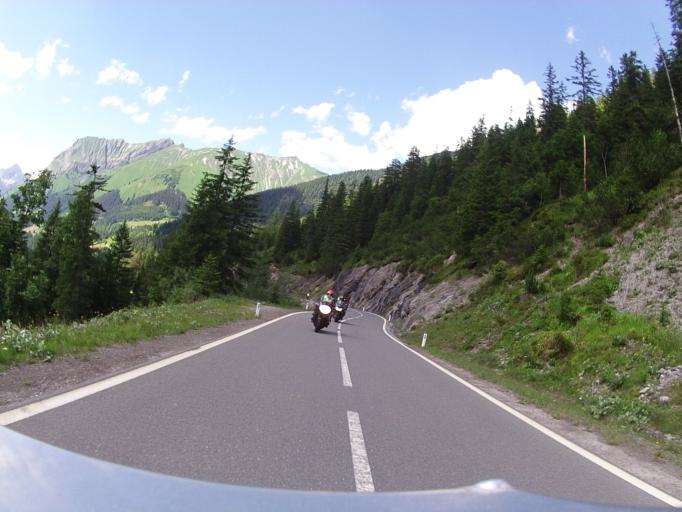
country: AT
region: Tyrol
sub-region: Politischer Bezirk Reutte
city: Gramais
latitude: 47.2933
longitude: 10.6035
